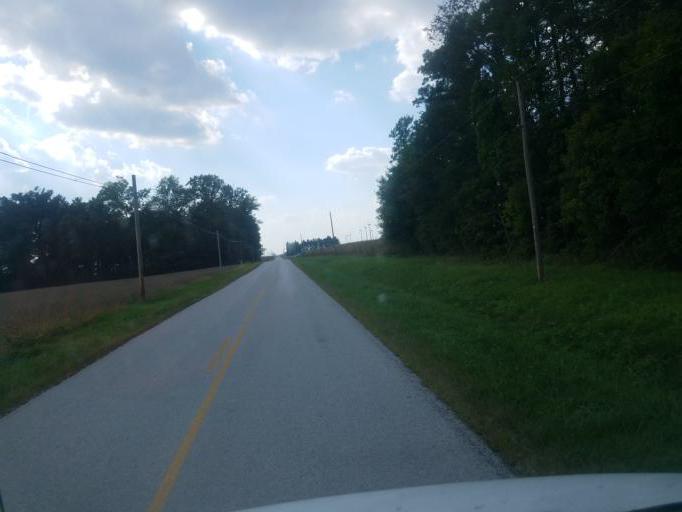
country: US
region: Ohio
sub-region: Hancock County
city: Arlington
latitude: 40.7907
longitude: -83.6873
